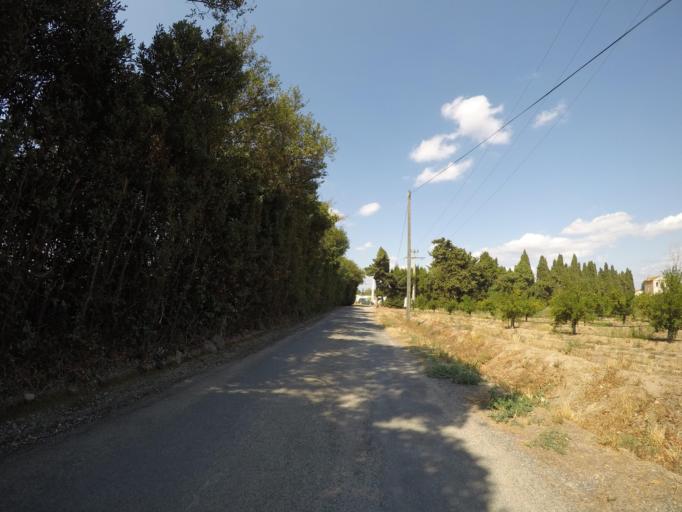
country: FR
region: Languedoc-Roussillon
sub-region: Departement des Pyrenees-Orientales
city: Saint-Esteve
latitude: 42.7033
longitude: 2.8592
